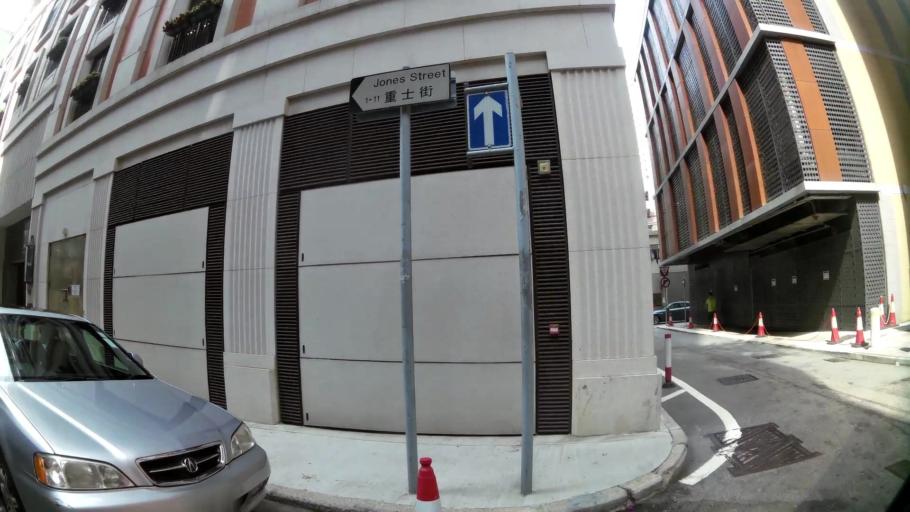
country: HK
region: Wanchai
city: Wan Chai
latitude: 22.2784
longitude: 114.1913
